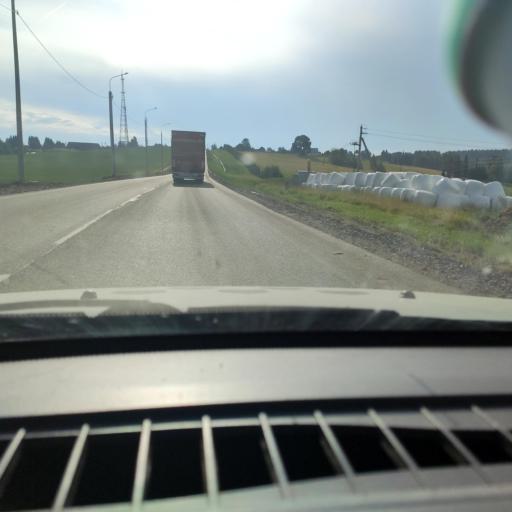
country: RU
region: Kirov
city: Kostino
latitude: 58.8510
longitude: 53.2760
